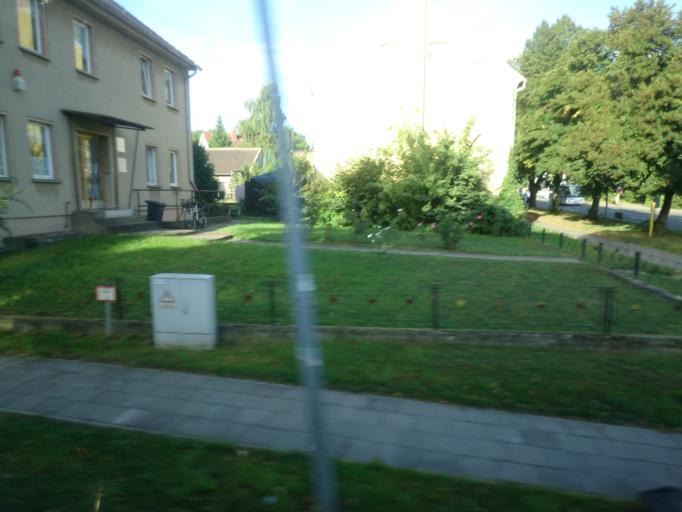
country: DE
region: Mecklenburg-Vorpommern
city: Anklam
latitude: 53.8544
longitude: 13.7043
